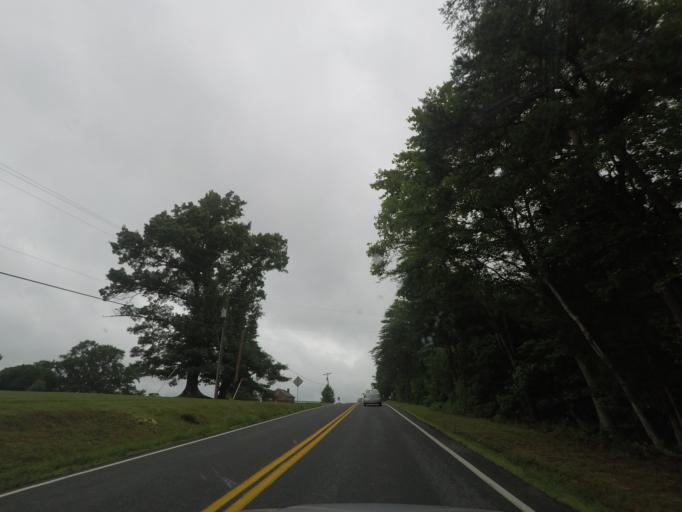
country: US
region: Virginia
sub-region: Fluvanna County
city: Palmyra
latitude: 37.8677
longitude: -78.2621
